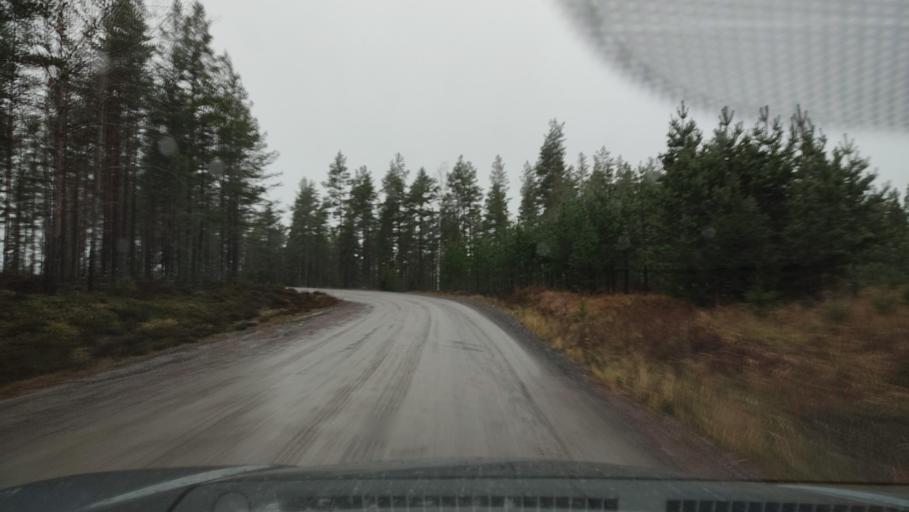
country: FI
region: Southern Ostrobothnia
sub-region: Suupohja
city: Karijoki
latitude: 62.1381
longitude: 21.6573
